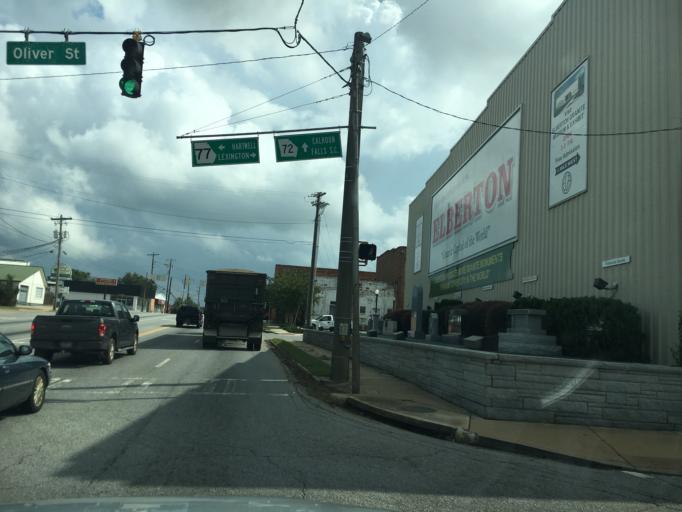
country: US
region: Georgia
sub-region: Elbert County
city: Elberton
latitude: 34.1109
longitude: -82.8677
